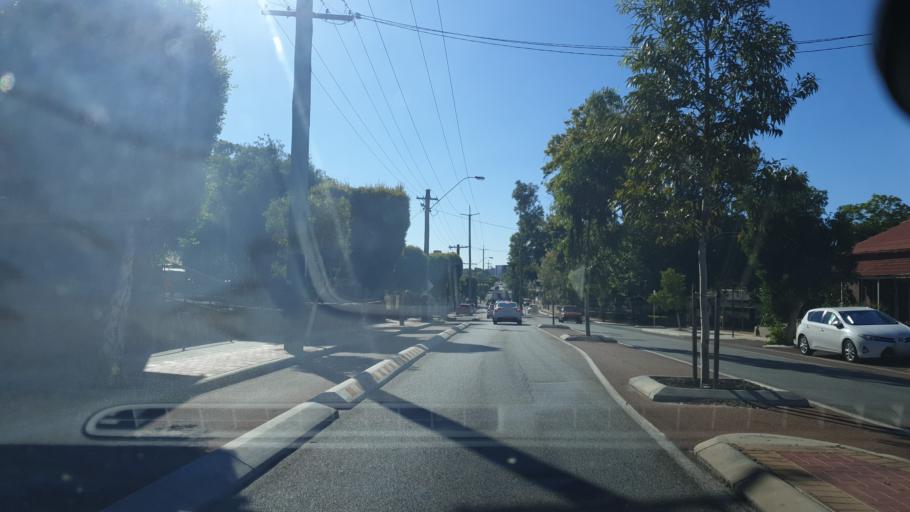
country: AU
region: Western Australia
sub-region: Vincent
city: Mount Lawley
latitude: -31.9418
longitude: 115.8654
